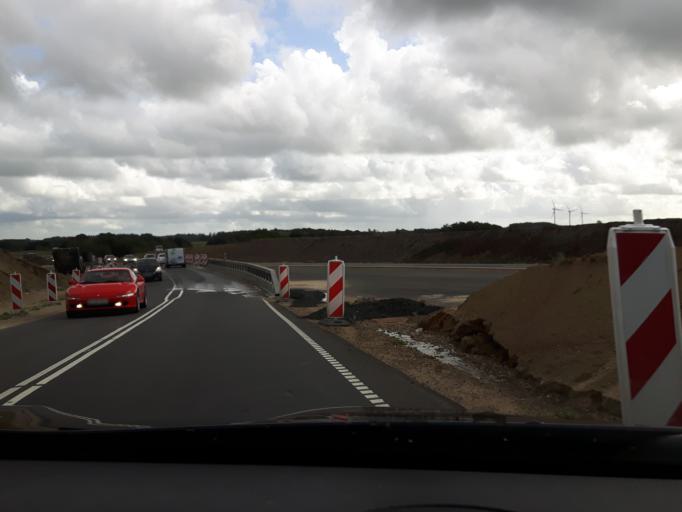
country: DK
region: Central Jutland
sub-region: Herning Kommune
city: Avlum
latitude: 56.2419
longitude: 8.8026
